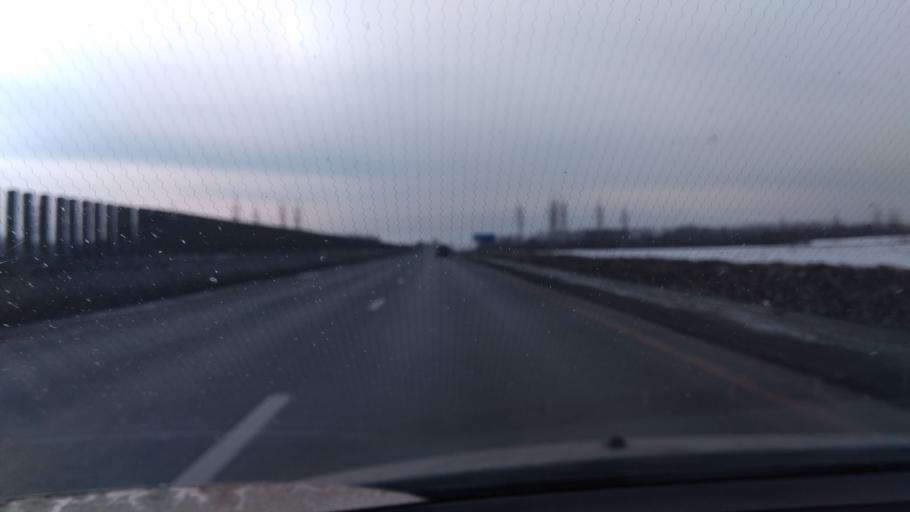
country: RU
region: Perm
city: Ferma
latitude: 57.9302
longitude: 56.3114
